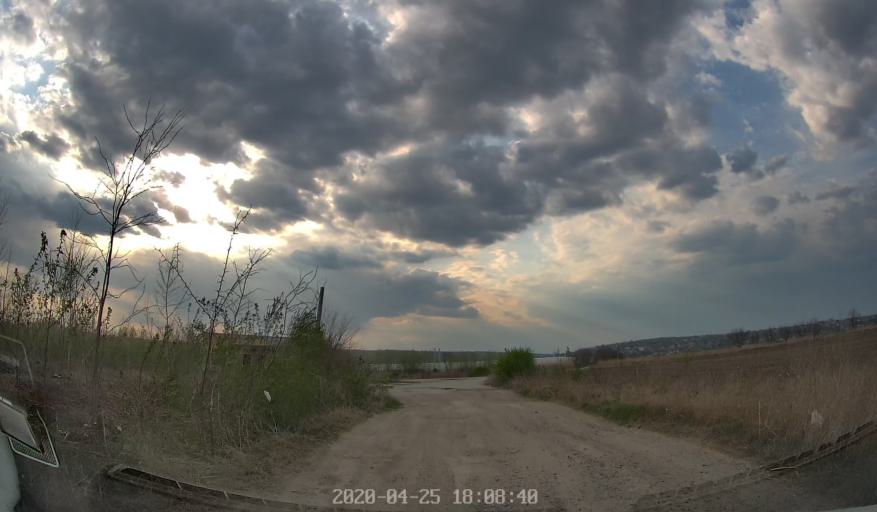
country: MD
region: Chisinau
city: Vadul lui Voda
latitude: 47.1295
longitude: 29.0818
